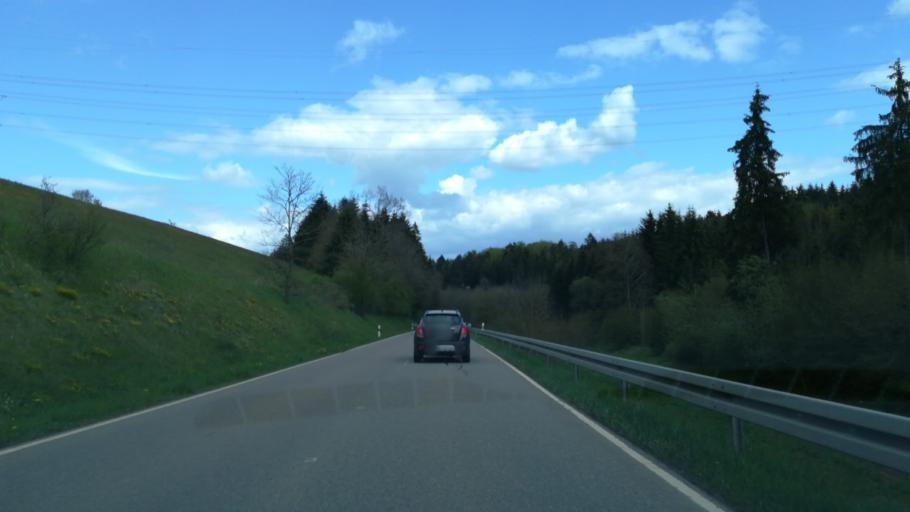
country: DE
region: Baden-Wuerttemberg
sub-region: Freiburg Region
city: Bonndorf im Schwarzwald
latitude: 47.8275
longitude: 8.4105
